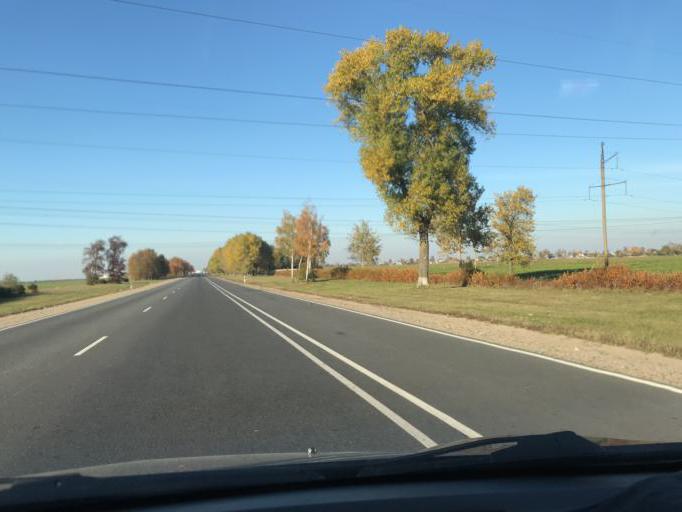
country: BY
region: Minsk
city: Slutsk
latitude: 53.0572
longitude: 27.5536
